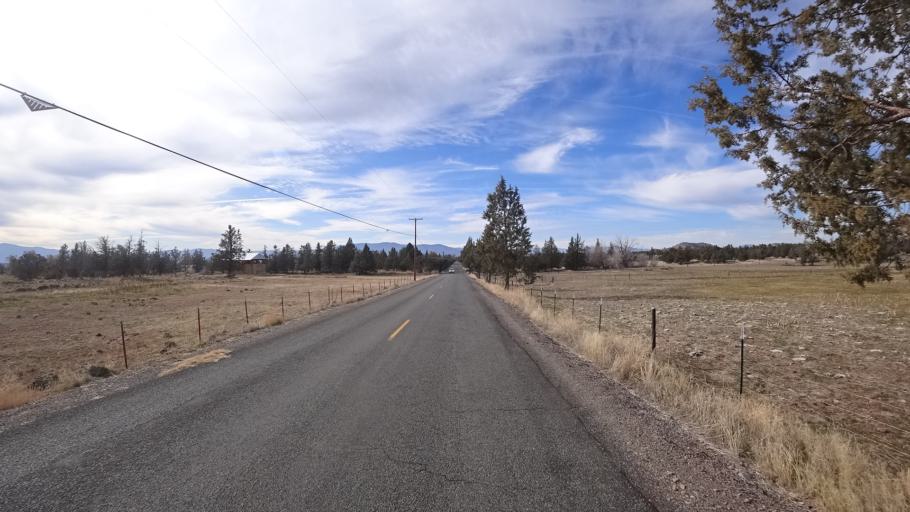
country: US
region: California
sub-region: Siskiyou County
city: Montague
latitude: 41.6382
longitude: -122.4058
